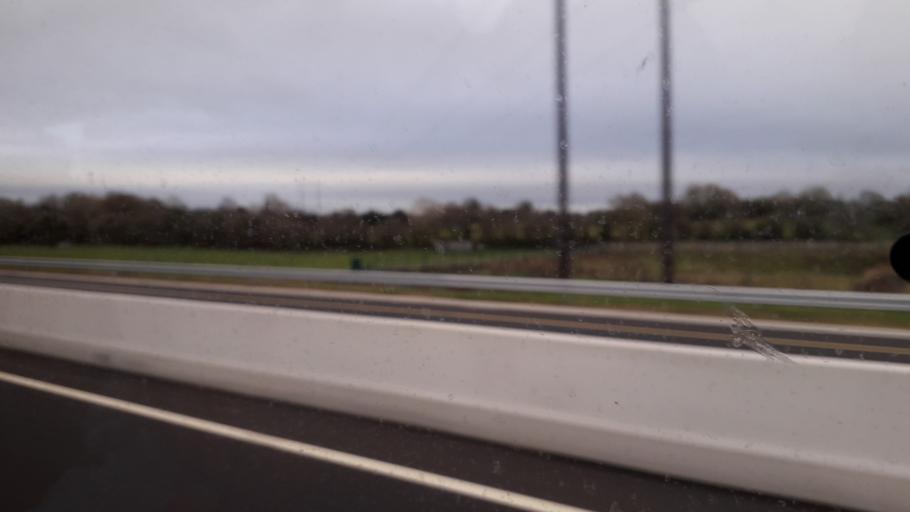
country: IE
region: Connaught
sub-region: County Galway
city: Athenry
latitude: 53.2652
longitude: -8.8147
